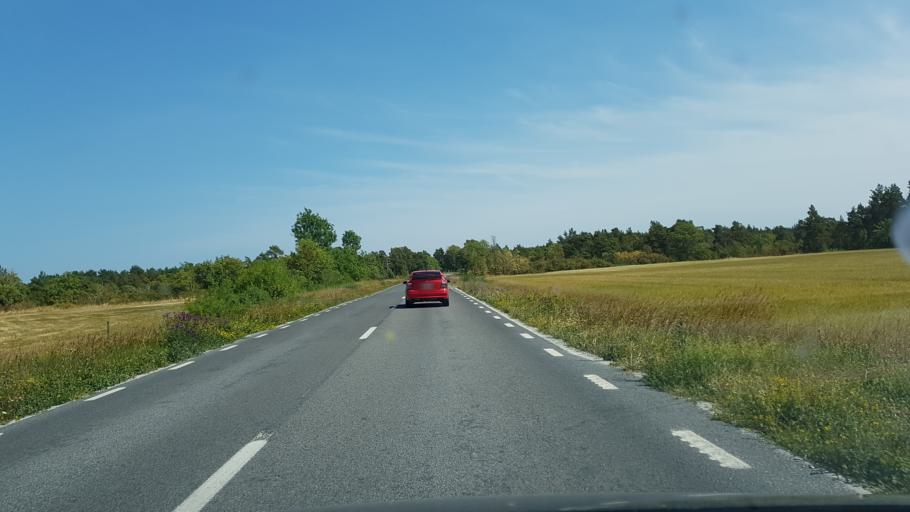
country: SE
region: Gotland
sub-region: Gotland
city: Visby
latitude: 57.6394
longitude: 18.5004
